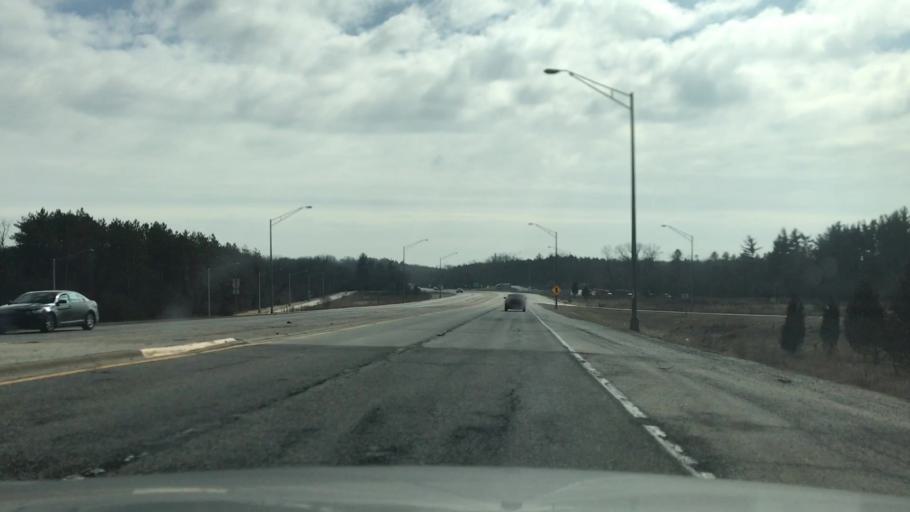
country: US
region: Illinois
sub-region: DuPage County
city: Darien
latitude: 41.7297
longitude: -87.9729
